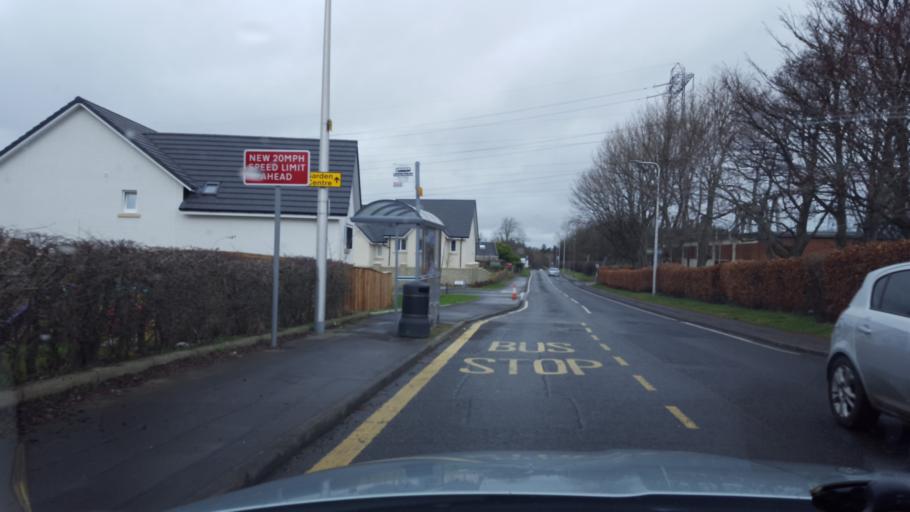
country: GB
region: Scotland
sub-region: Edinburgh
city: Currie
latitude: 55.9010
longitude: -3.3100
